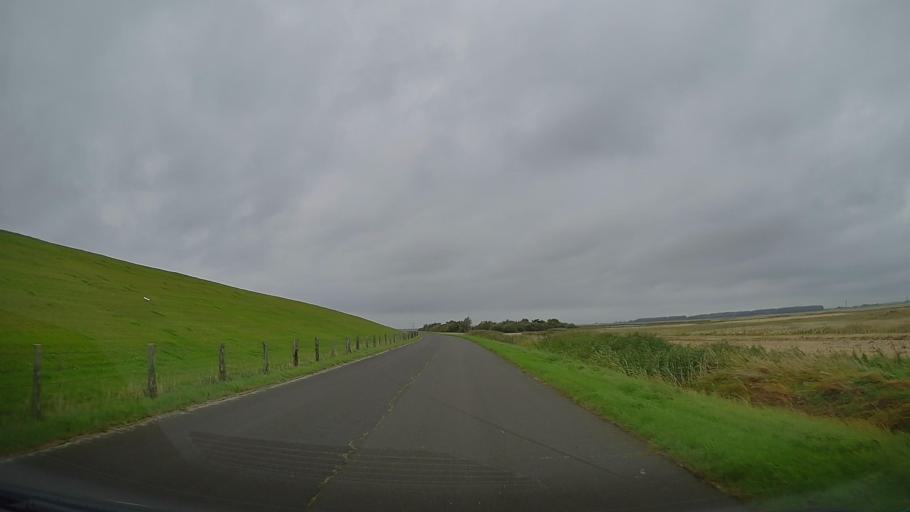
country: DE
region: Schleswig-Holstein
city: Busenwurth
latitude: 54.0454
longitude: 8.9826
